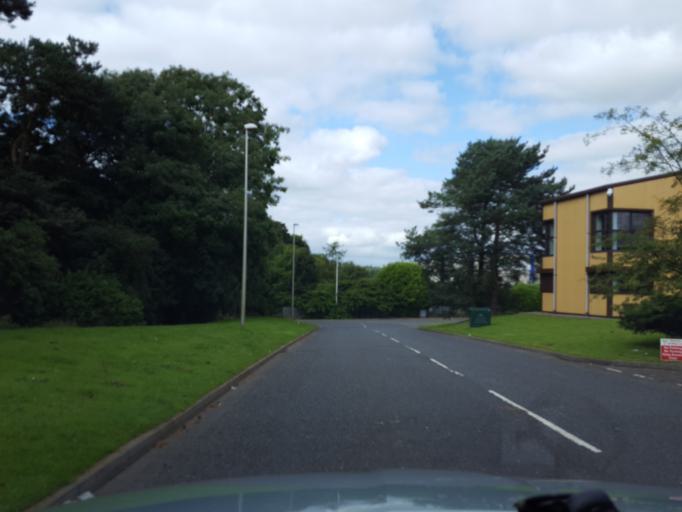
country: GB
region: Scotland
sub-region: West Lothian
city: Livingston
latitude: 55.9095
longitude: -3.5676
